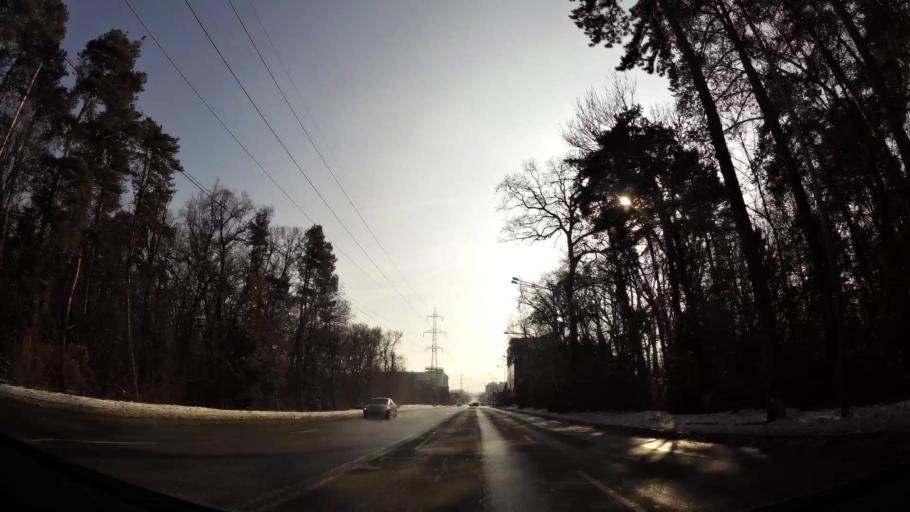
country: BG
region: Sofia-Capital
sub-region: Stolichna Obshtina
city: Sofia
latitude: 42.6609
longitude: 23.3368
